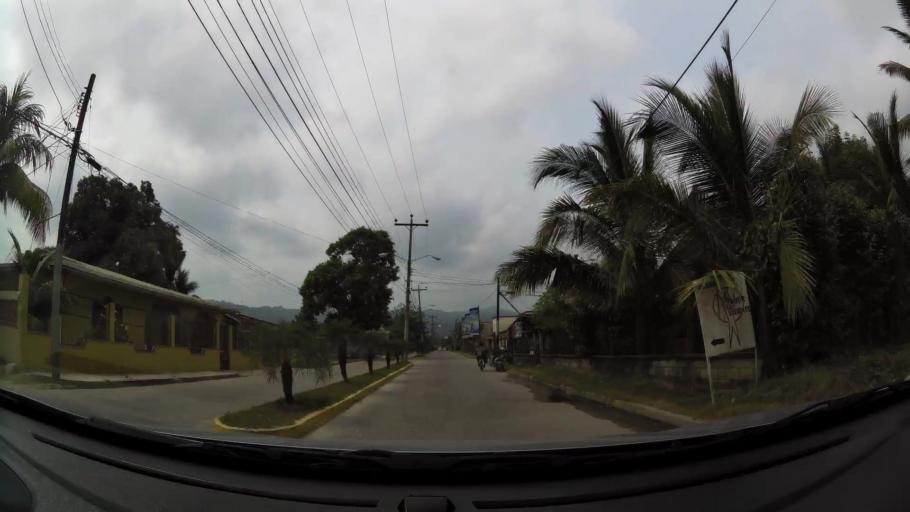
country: HN
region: Atlantida
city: Tela
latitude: 15.7687
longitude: -87.4814
